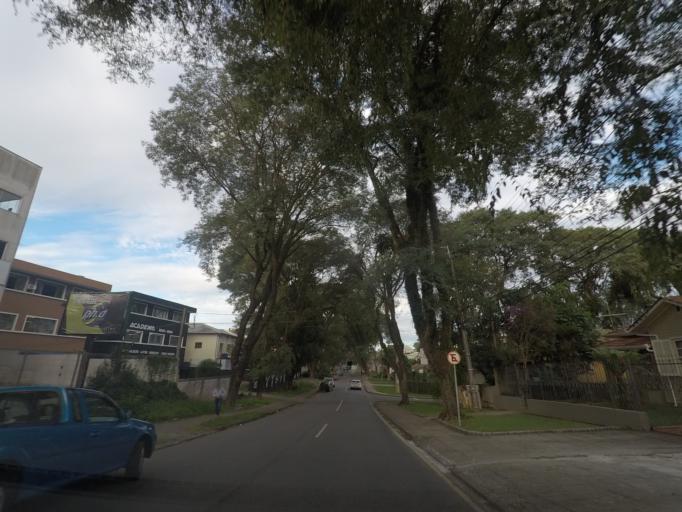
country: BR
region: Parana
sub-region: Curitiba
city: Curitiba
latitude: -25.4758
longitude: -49.2991
